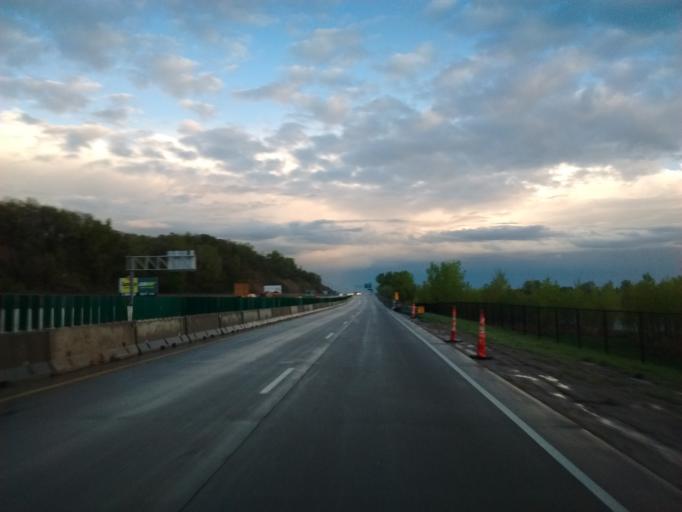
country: US
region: Nebraska
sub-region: Dakota County
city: South Sioux City
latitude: 42.4719
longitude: -96.3824
